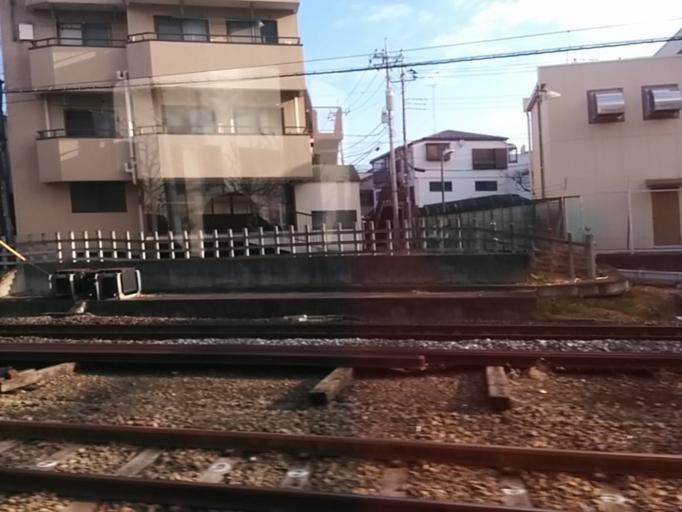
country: JP
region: Saitama
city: Kamifukuoka
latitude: 35.8753
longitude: 139.5106
